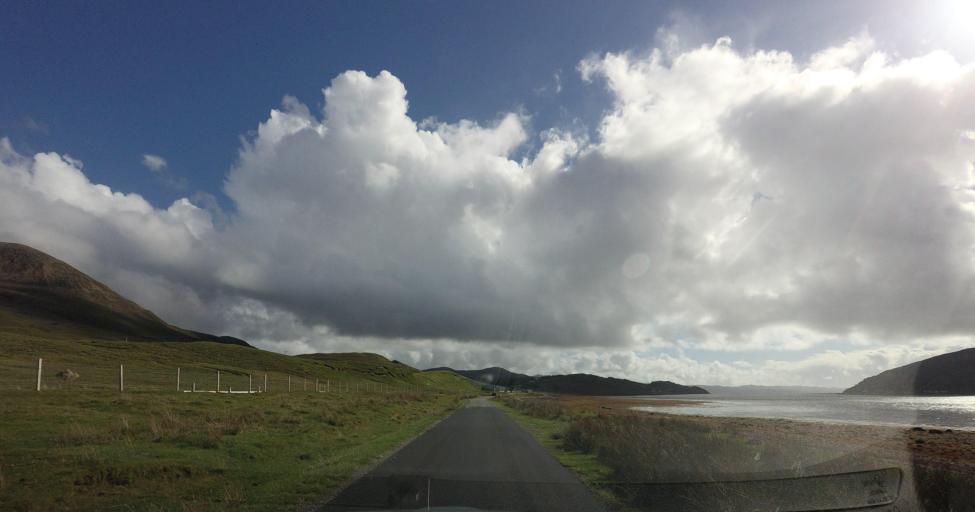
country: GB
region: Scotland
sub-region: Highland
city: Portree
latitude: 57.2213
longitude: -6.0297
